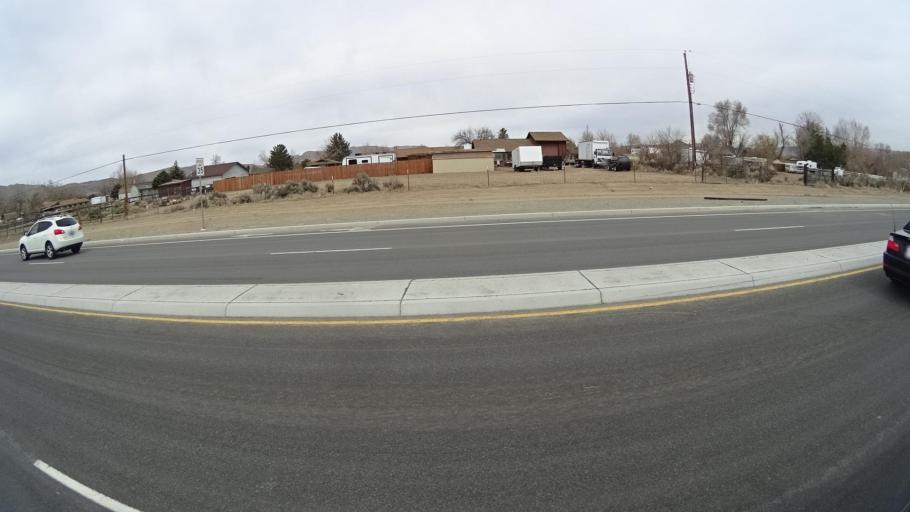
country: US
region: Nevada
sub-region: Washoe County
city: Spanish Springs
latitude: 39.6361
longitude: -119.7028
